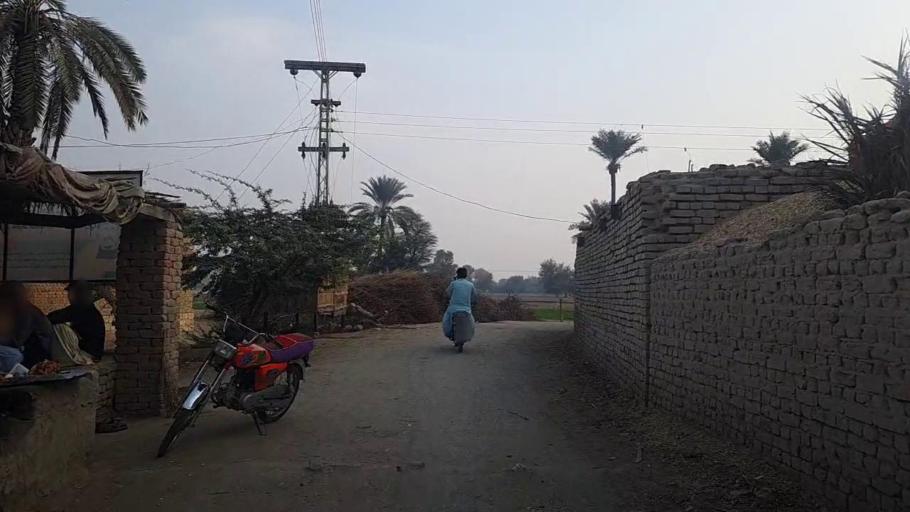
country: PK
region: Sindh
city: Kot Diji
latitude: 27.3755
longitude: 68.6660
